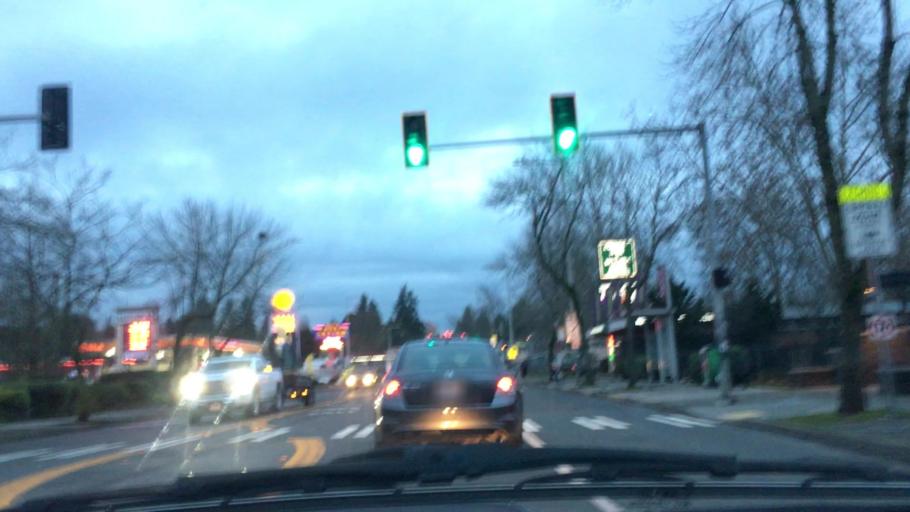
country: US
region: Washington
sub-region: King County
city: White Center
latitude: 47.5175
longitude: -122.3676
